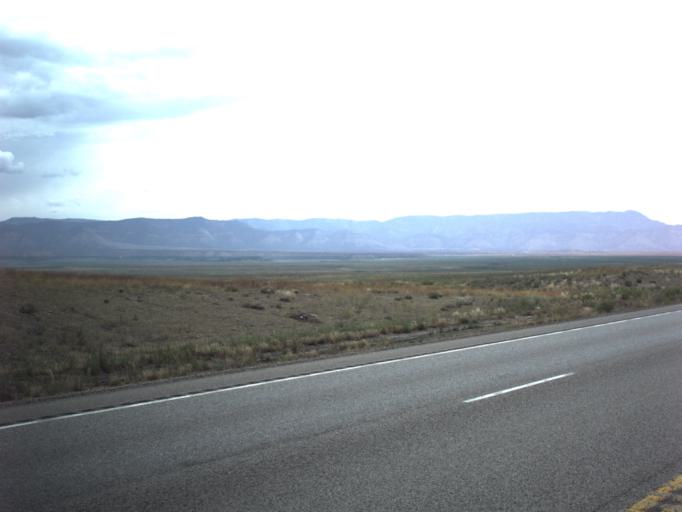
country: US
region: Utah
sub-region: Carbon County
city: Wellington
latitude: 39.5394
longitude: -110.6051
